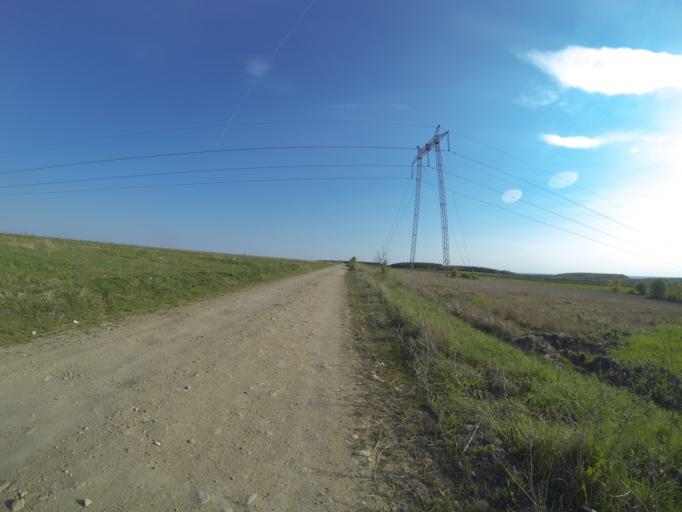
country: RO
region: Dolj
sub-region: Comuna Filiasi
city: Fratostita
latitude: 44.5674
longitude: 23.5881
